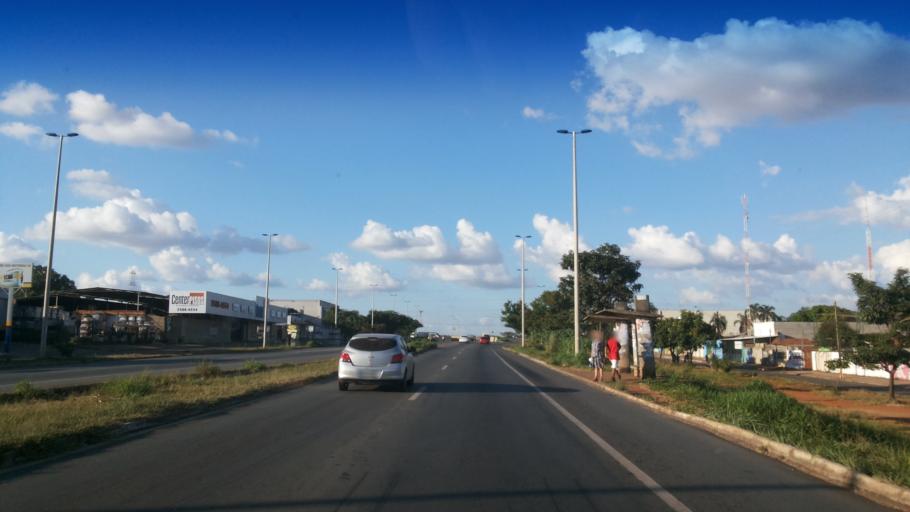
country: BR
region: Goias
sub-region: Goiania
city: Goiania
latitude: -16.7565
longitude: -49.3402
